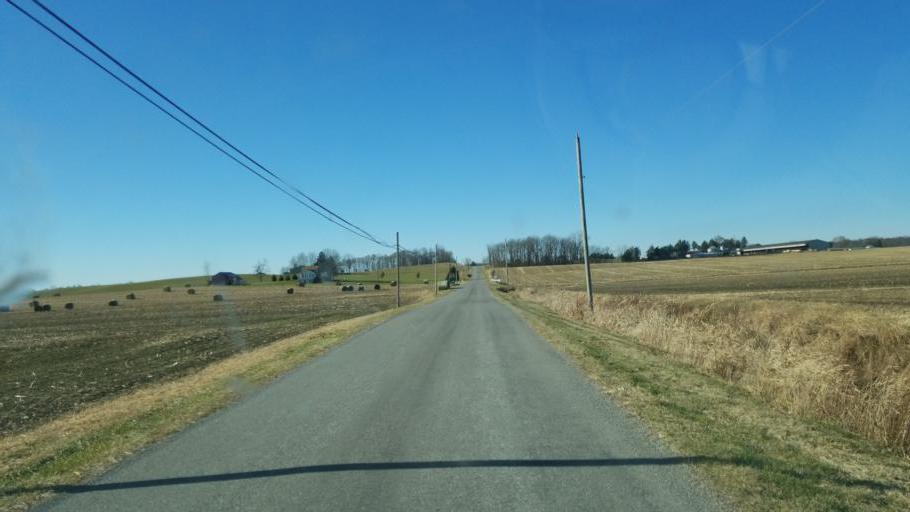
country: US
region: Ohio
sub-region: Richland County
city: Shelby
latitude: 40.9381
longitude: -82.5911
